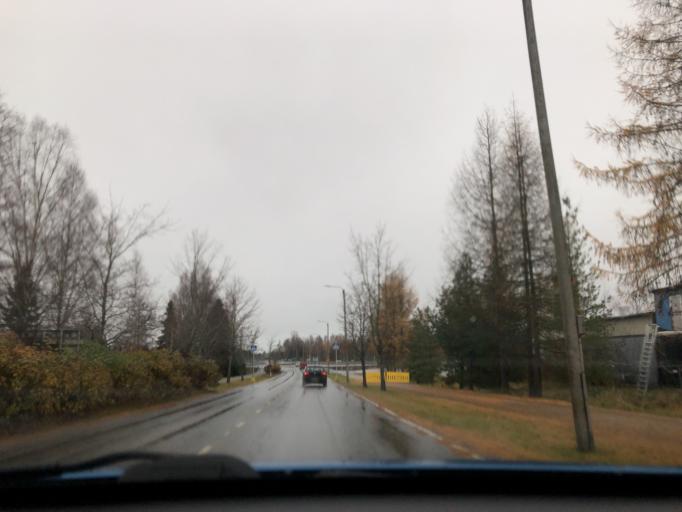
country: FI
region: Pirkanmaa
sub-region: Tampere
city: Kangasala
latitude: 61.4675
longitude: 24.0389
